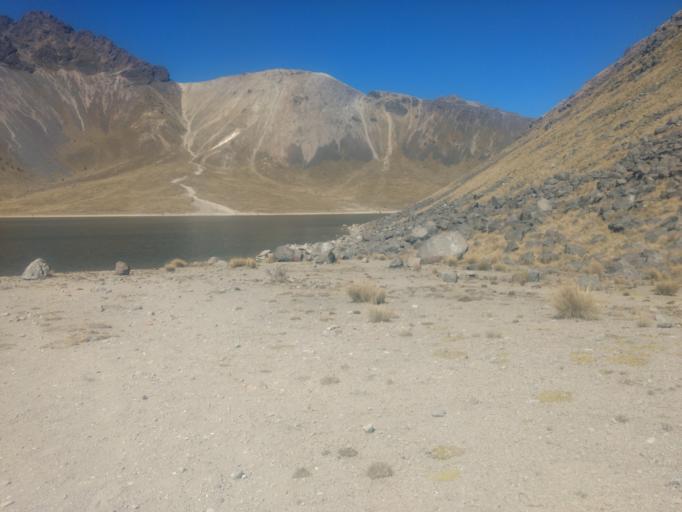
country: MX
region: Mexico
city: Cerro La Calera
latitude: 19.1070
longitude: -99.7578
